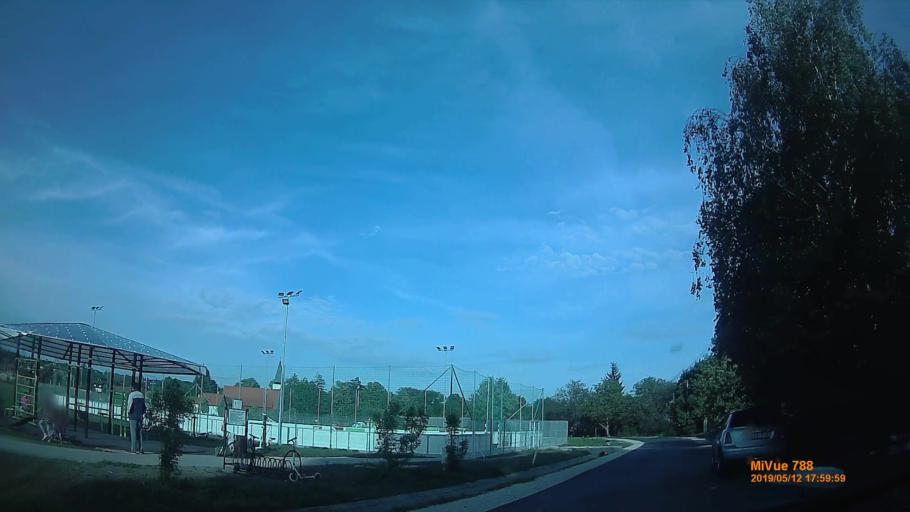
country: HU
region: Pest
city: Pilisszentivan
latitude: 47.5773
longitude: 18.8805
